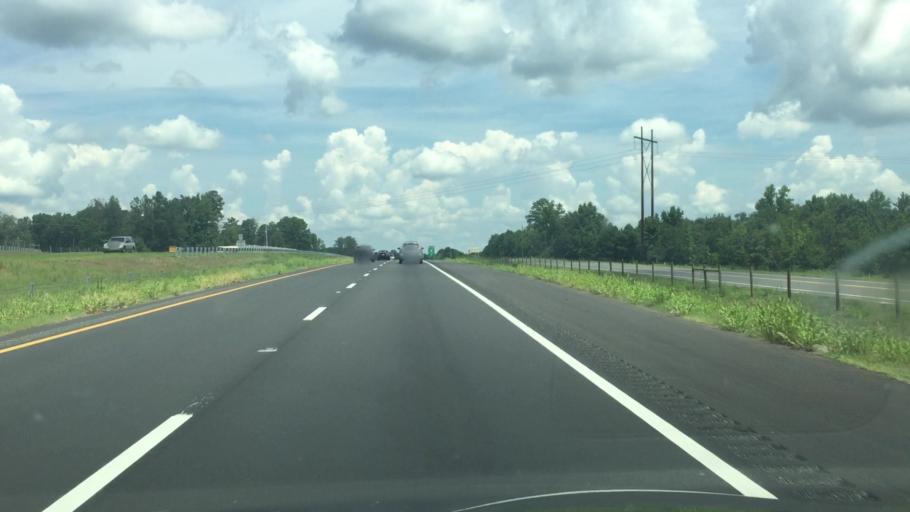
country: US
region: North Carolina
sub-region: Richmond County
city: Ellerbe
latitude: 35.0344
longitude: -79.7690
